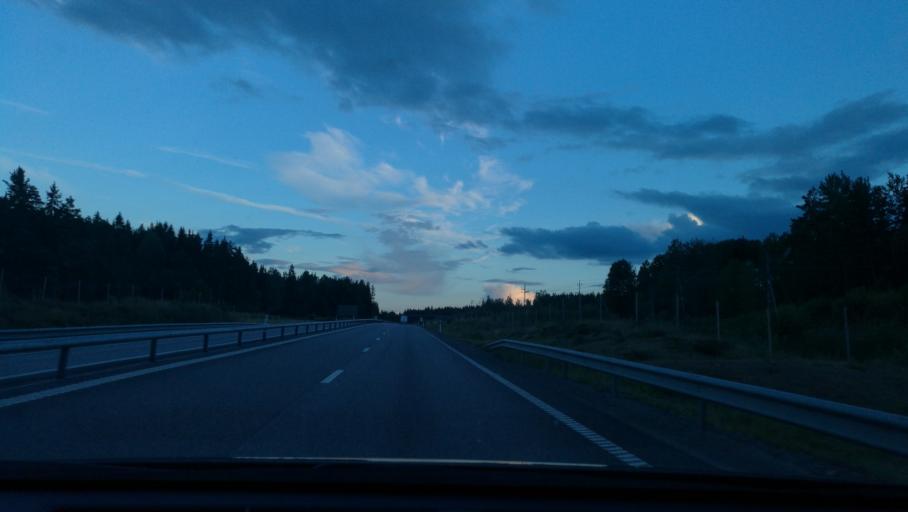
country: SE
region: Soedermanland
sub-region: Katrineholms Kommun
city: Katrineholm
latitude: 58.9299
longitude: 16.1960
